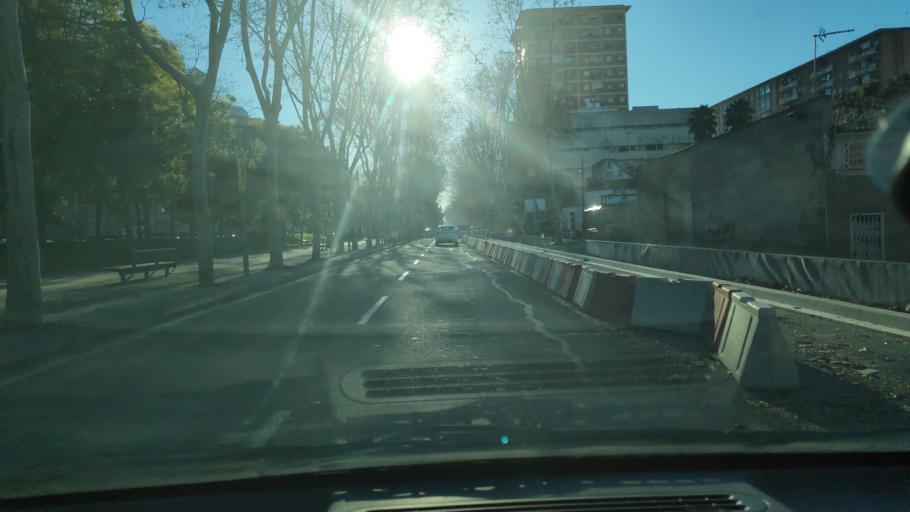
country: ES
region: Catalonia
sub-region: Provincia de Barcelona
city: Sant Marti
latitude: 41.4174
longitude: 2.2109
